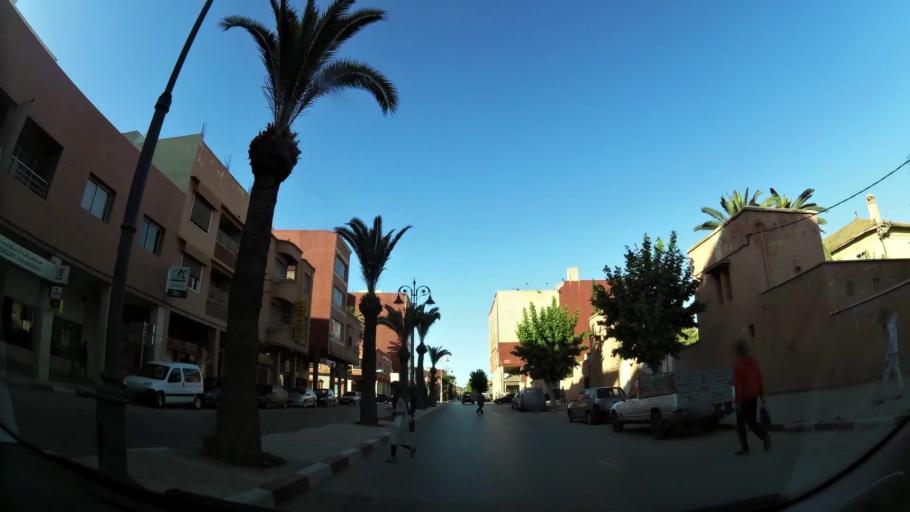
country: MA
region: Oriental
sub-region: Berkane-Taourirt
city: Berkane
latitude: 34.9253
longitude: -2.3335
